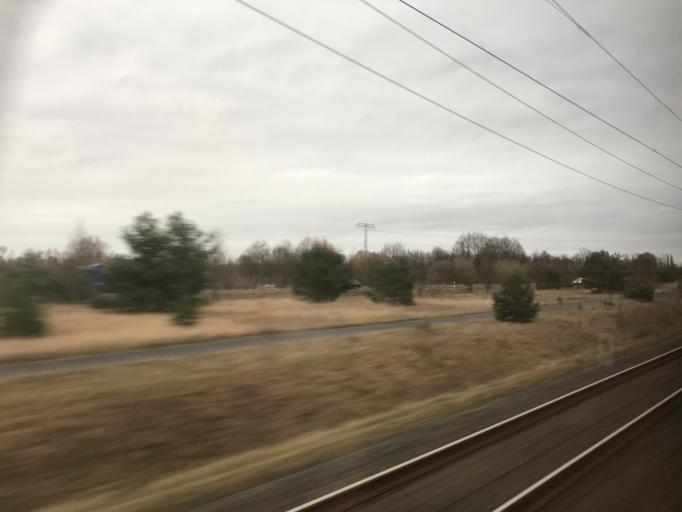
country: DE
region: Saxony-Anhalt
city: Stendal
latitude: 52.5726
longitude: 11.8436
